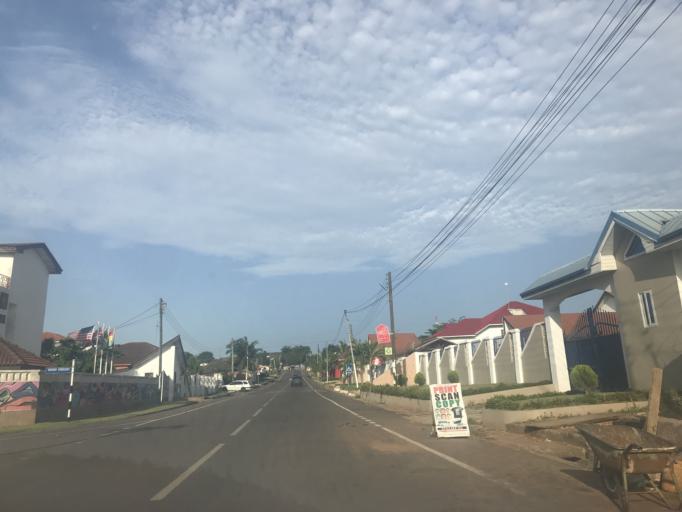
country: GH
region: Greater Accra
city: Medina Estates
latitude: 5.6688
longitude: -0.1809
